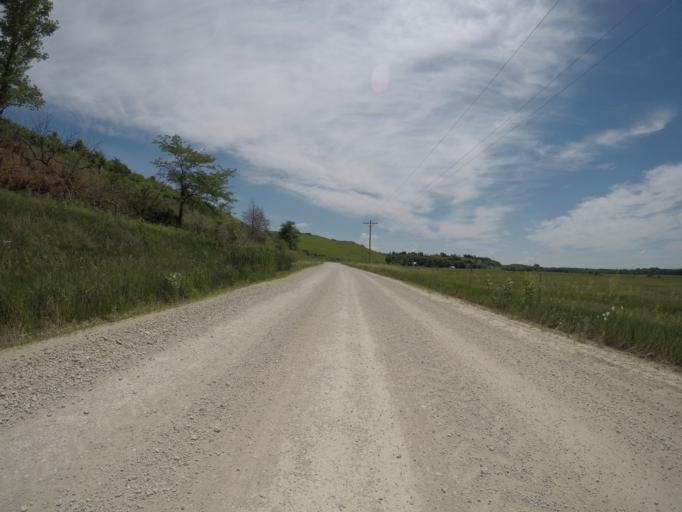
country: US
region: Kansas
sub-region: Wabaunsee County
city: Alma
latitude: 38.9888
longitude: -96.2695
